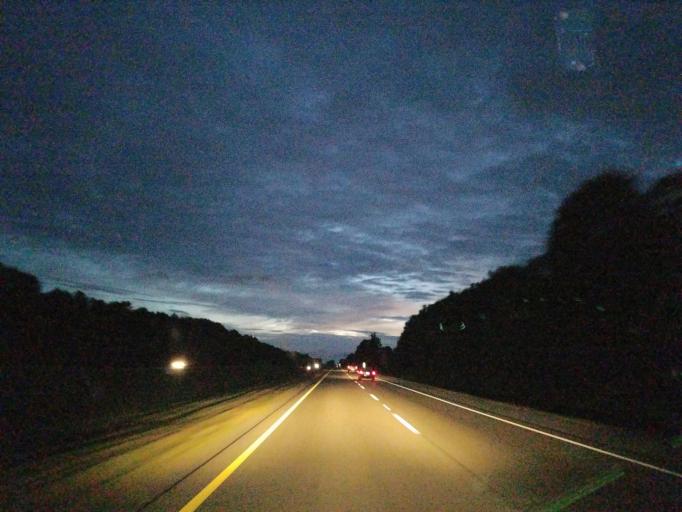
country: US
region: Mississippi
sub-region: Jones County
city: Sharon
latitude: 31.7527
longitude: -89.0728
